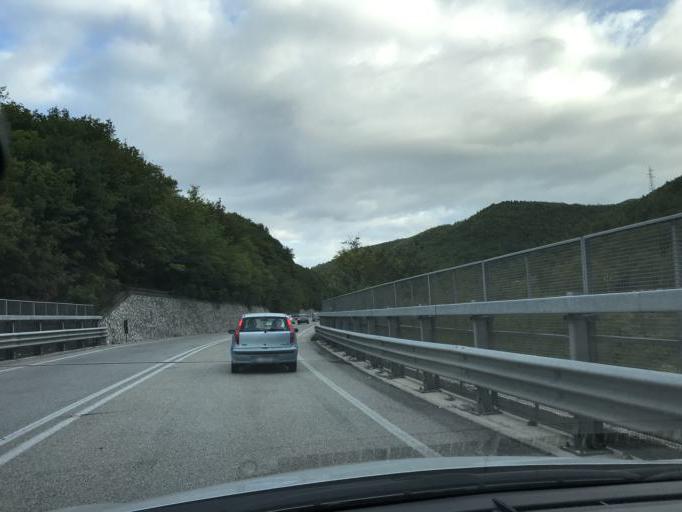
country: IT
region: Umbria
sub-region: Provincia di Perugia
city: Spoleto
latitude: 42.6766
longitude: 12.7254
